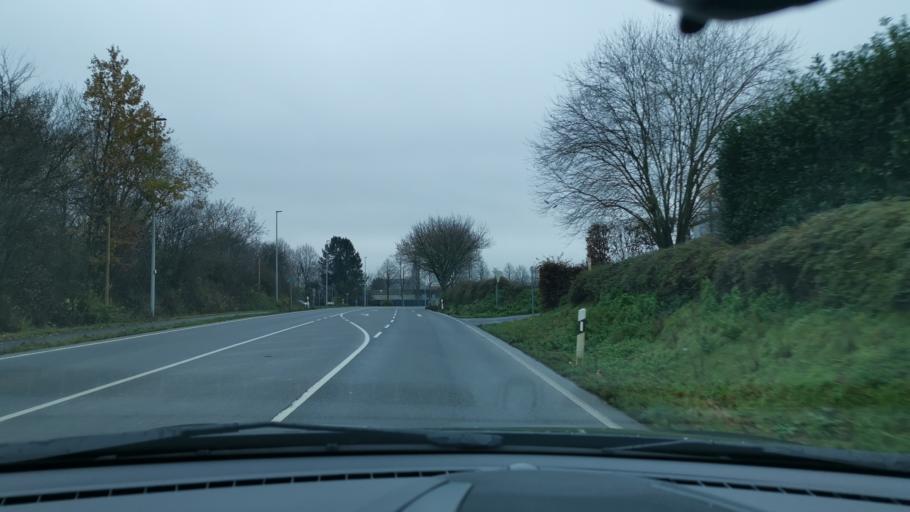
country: DE
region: North Rhine-Westphalia
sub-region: Regierungsbezirk Dusseldorf
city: Juchen
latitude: 51.1082
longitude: 6.5003
